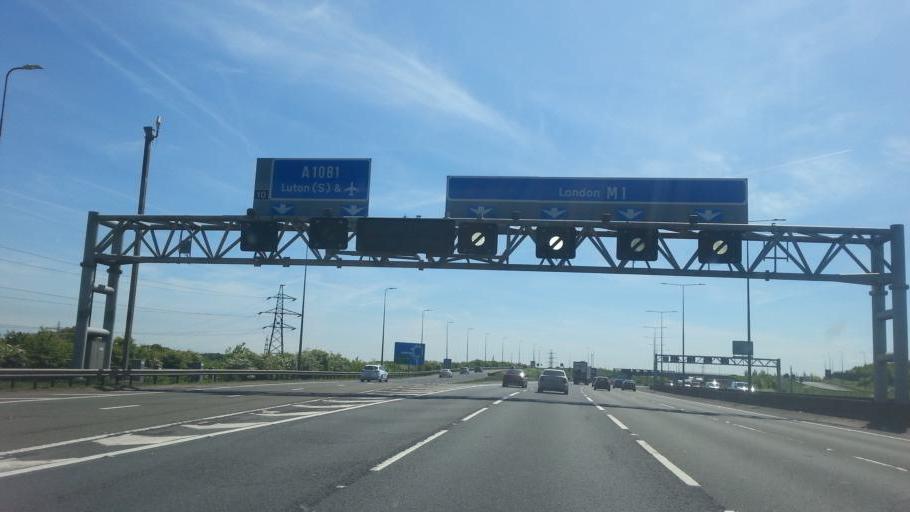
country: GB
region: England
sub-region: Luton
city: Luton
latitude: 51.8580
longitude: -0.4272
